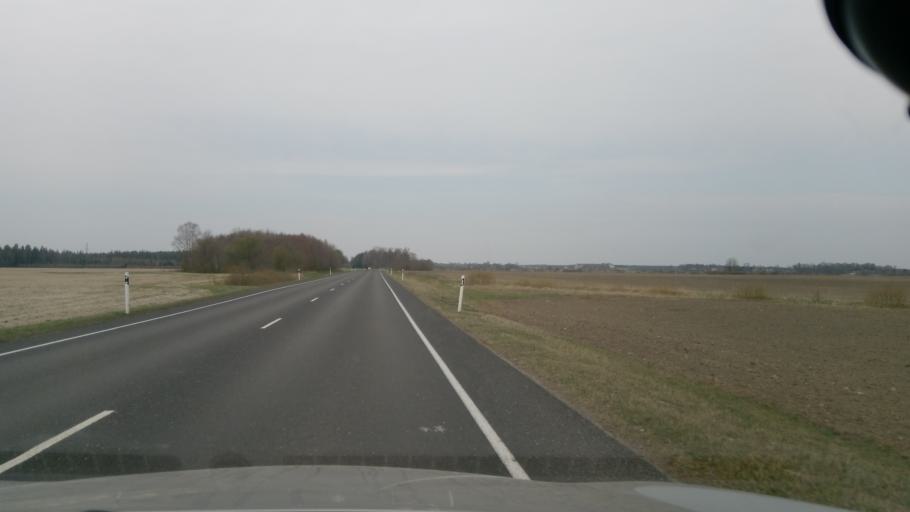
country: EE
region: Viljandimaa
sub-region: Vohma linn
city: Vohma
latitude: 58.7330
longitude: 25.5919
